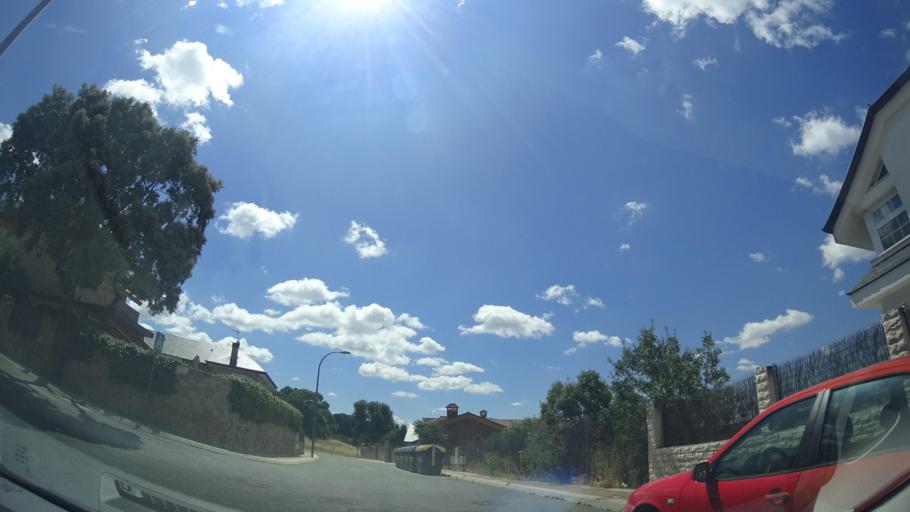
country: ES
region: Madrid
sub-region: Provincia de Madrid
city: Collado-Villalba
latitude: 40.6232
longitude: -3.9933
